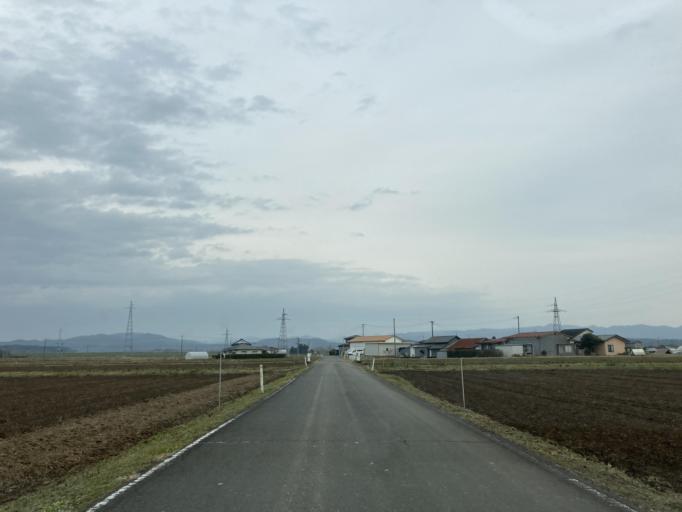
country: JP
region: Miyagi
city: Wakuya
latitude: 38.7121
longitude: 141.2555
